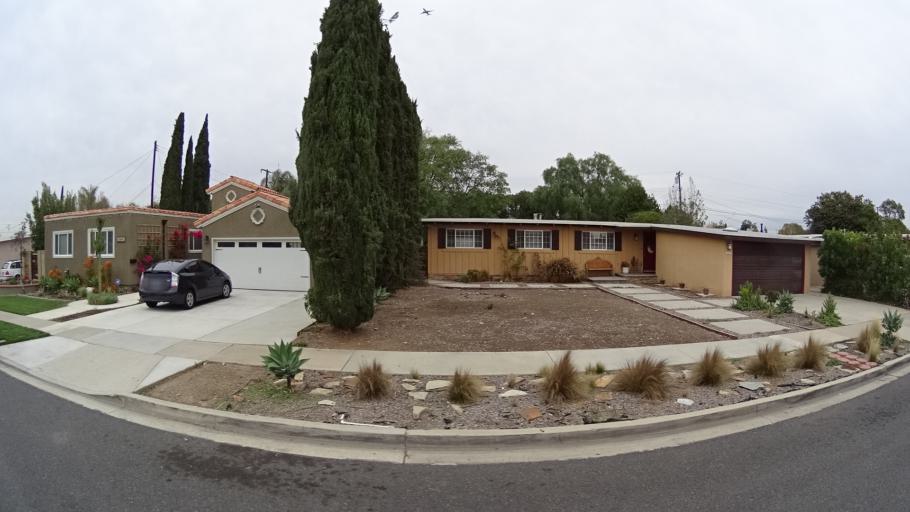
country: US
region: California
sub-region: Orange County
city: Tustin
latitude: 33.7539
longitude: -117.8172
